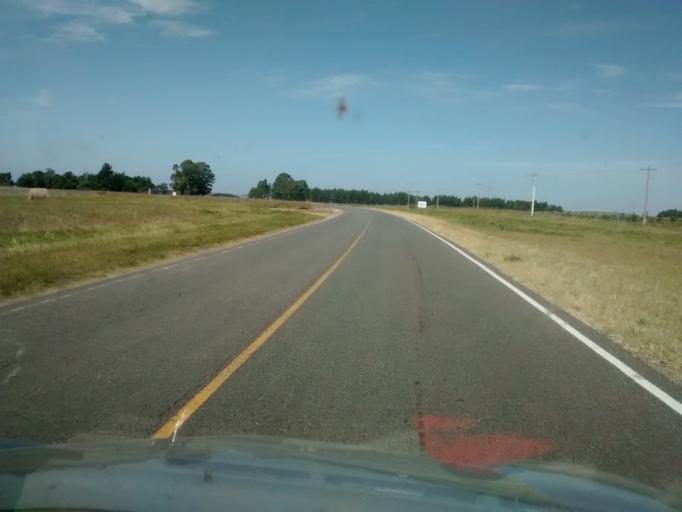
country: AR
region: Buenos Aires
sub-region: Partido de Balcarce
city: Balcarce
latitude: -37.6429
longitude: -58.4894
